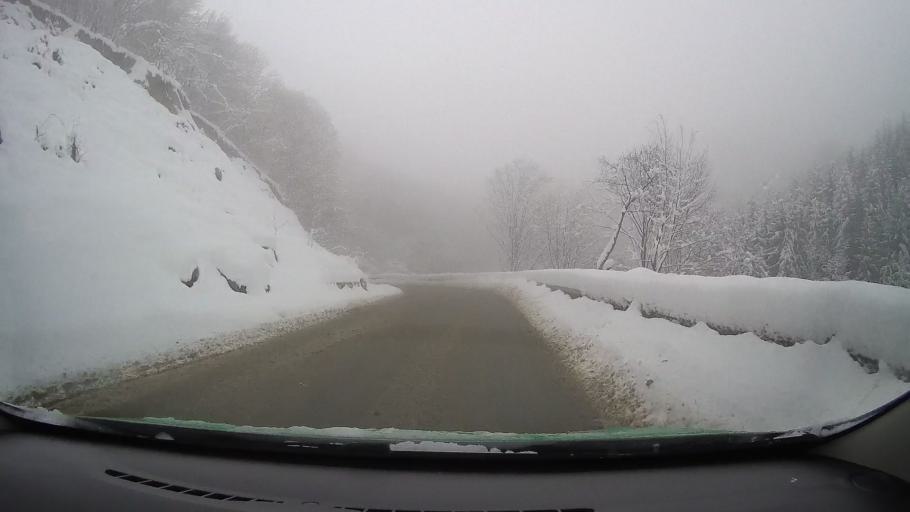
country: RO
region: Sibiu
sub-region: Comuna Tilisca
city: Tilisca
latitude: 45.7996
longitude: 23.7953
